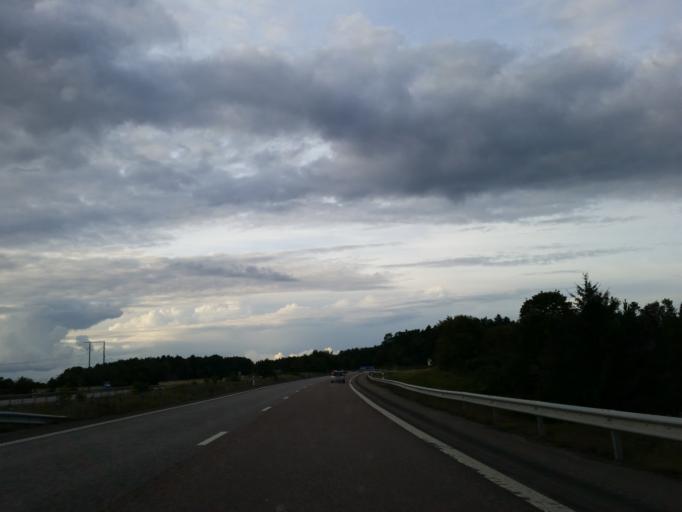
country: SE
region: Uppsala
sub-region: Knivsta Kommun
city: Knivsta
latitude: 59.7410
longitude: 17.8191
